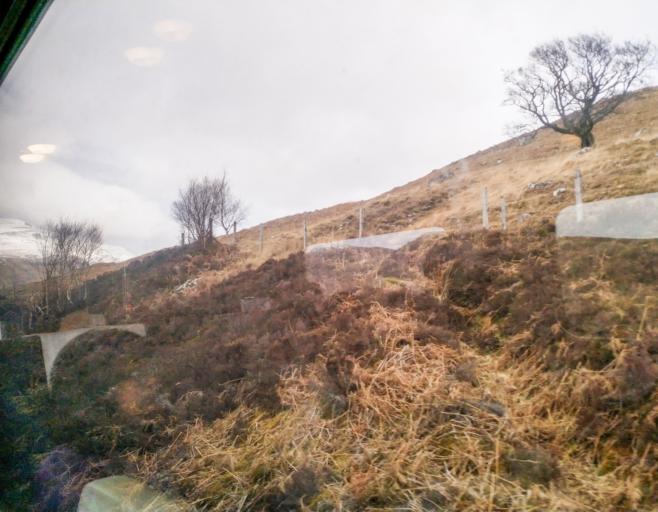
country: GB
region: Scotland
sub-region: Highland
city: Spean Bridge
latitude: 56.7774
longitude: -4.7310
